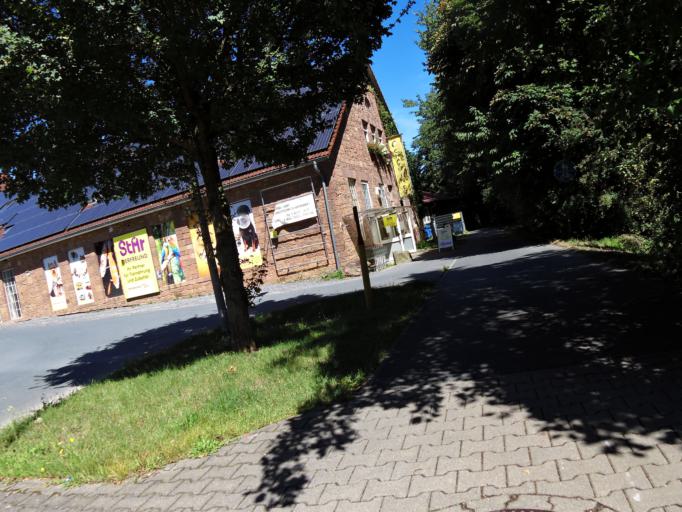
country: DE
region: Hesse
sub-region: Regierungsbezirk Darmstadt
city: Erbach
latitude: 49.6713
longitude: 8.9935
